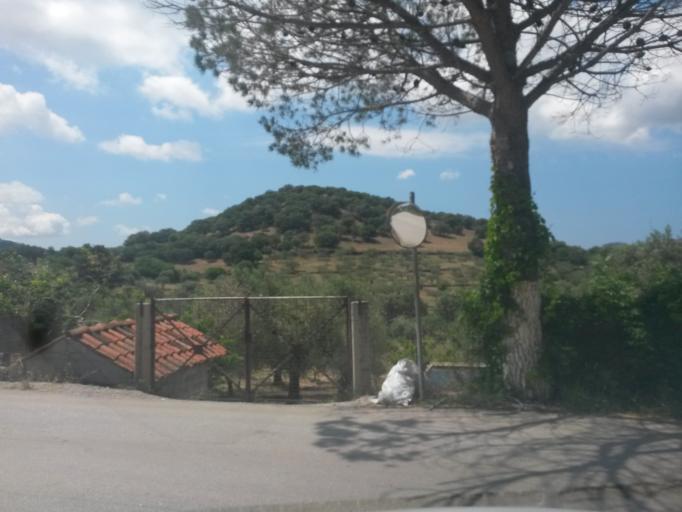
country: GR
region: North Aegean
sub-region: Nomos Lesvou
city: Eresos
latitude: 39.2287
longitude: 26.0511
